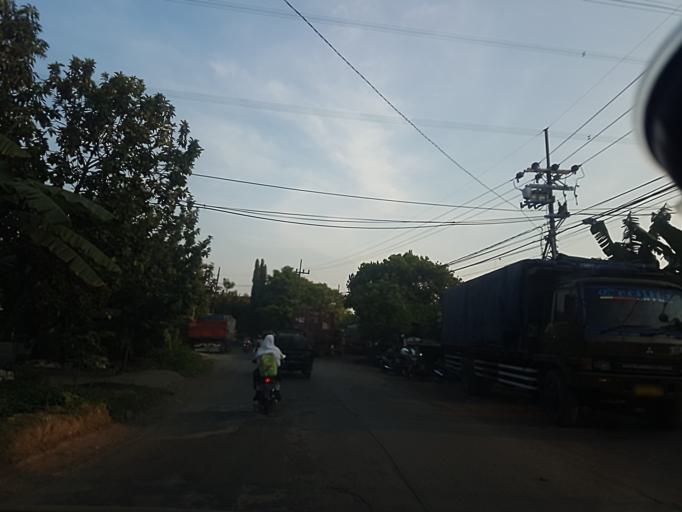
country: ID
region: East Java
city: Gresik
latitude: -7.1660
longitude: 112.6588
